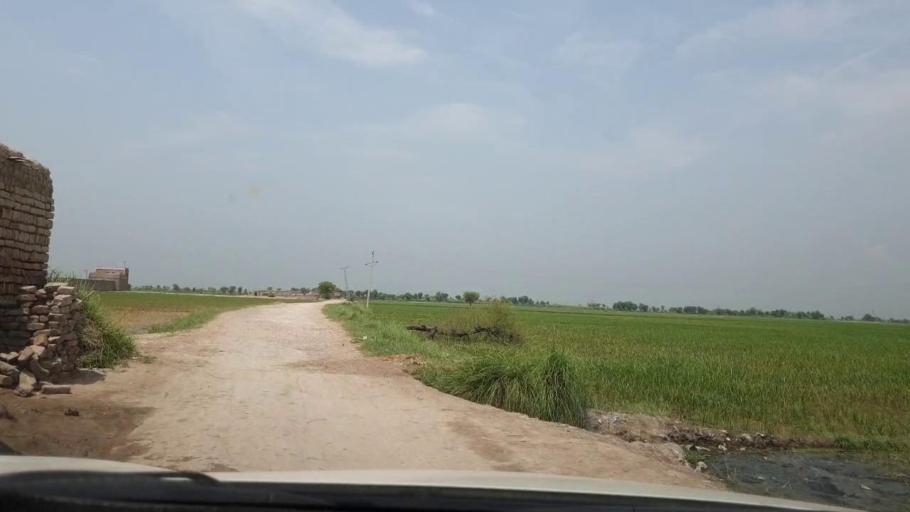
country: PK
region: Sindh
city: New Badah
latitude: 27.3916
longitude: 68.0454
